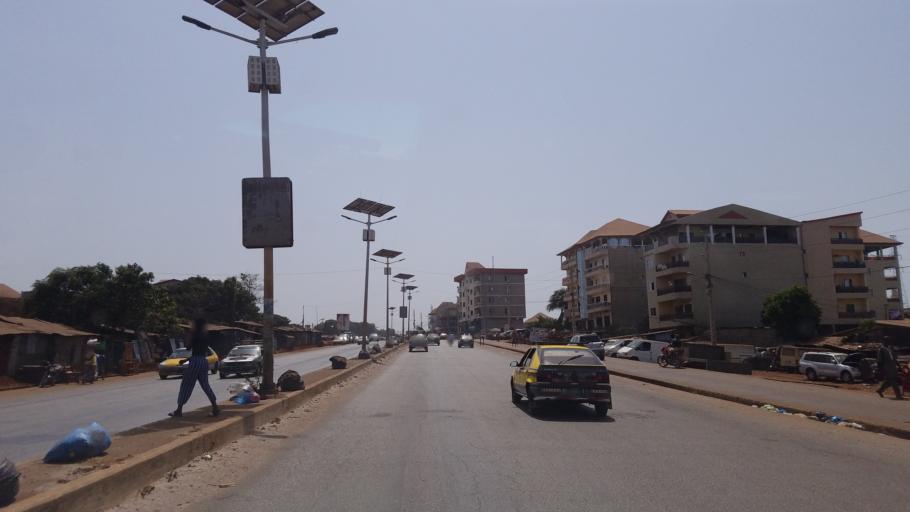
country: GN
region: Conakry
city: Conakry
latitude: 9.6495
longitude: -13.5834
